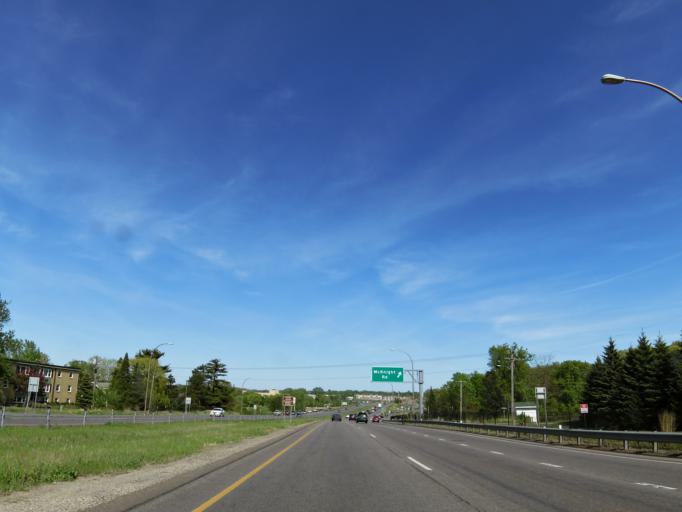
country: US
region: Minnesota
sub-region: Ramsey County
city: North Saint Paul
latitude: 45.0118
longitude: -93.0136
